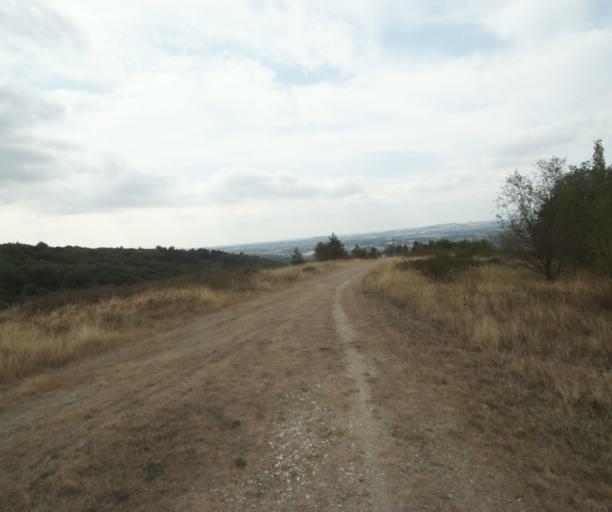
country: FR
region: Midi-Pyrenees
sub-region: Departement de la Haute-Garonne
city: Revel
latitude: 43.4437
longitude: 2.0116
